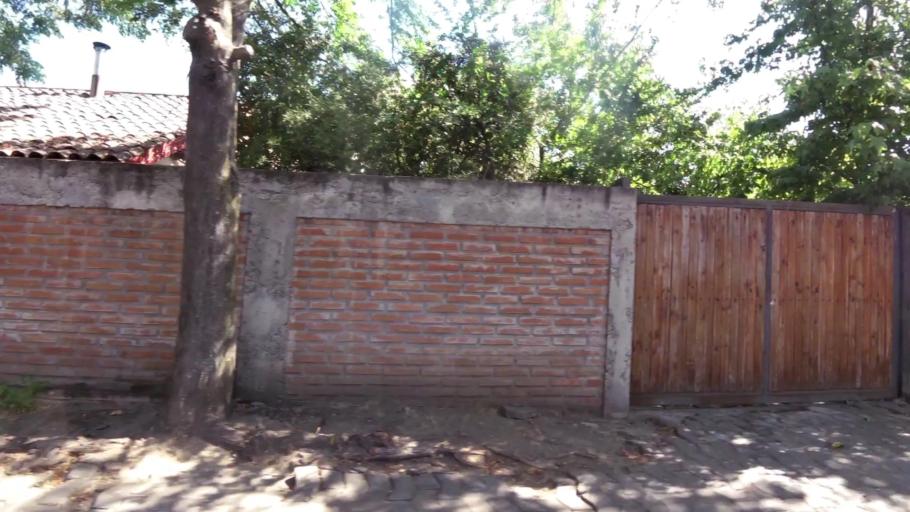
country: CL
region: Maule
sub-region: Provincia de Talca
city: Talca
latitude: -35.4324
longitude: -71.6210
